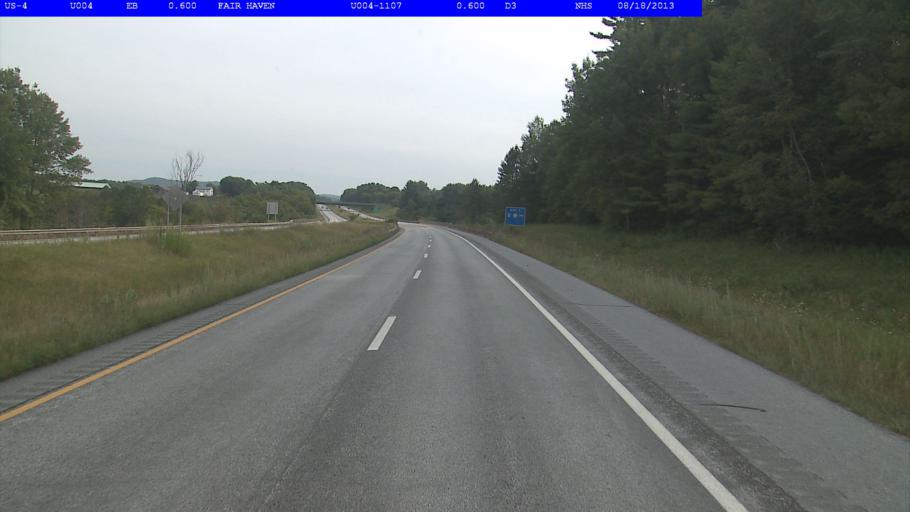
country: US
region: Vermont
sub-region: Rutland County
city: Fair Haven
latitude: 43.5915
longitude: -73.2859
